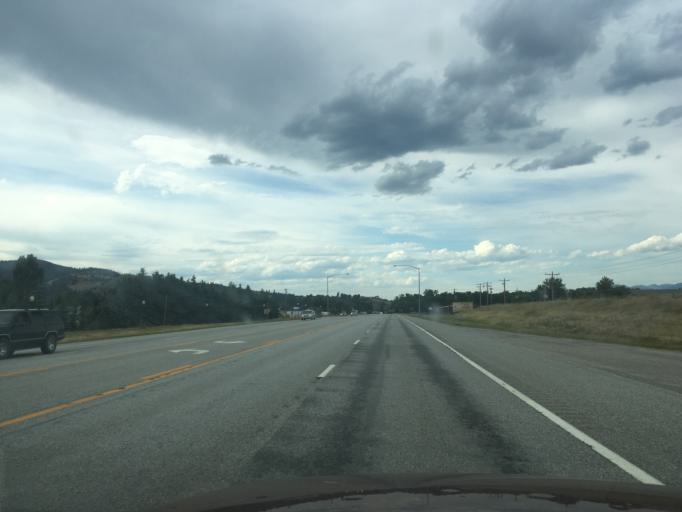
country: US
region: Montana
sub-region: Missoula County
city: Lolo
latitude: 46.7417
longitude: -114.0814
